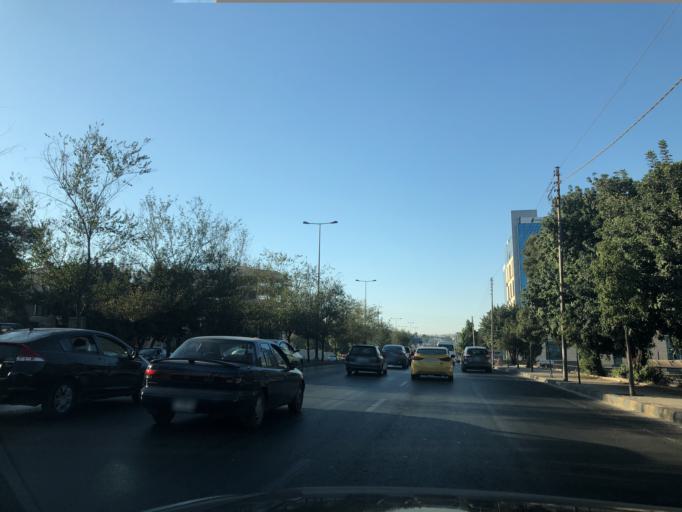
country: JO
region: Amman
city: Wadi as Sir
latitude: 31.9690
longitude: 35.8415
